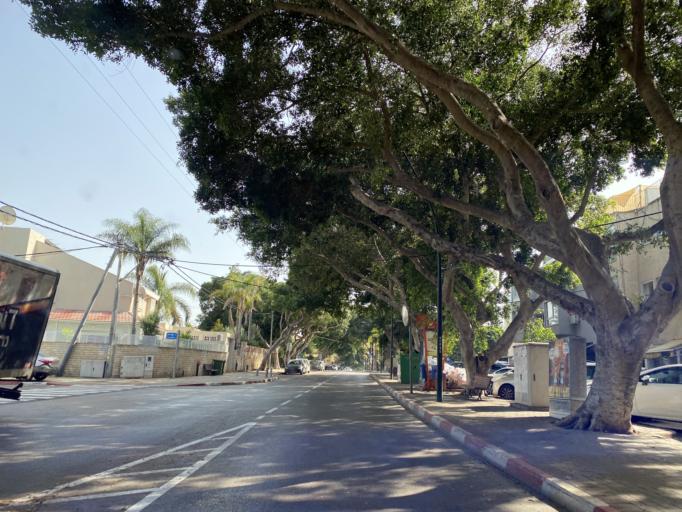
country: IL
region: Tel Aviv
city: Herzliya Pituah
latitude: 32.1737
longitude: 34.8082
